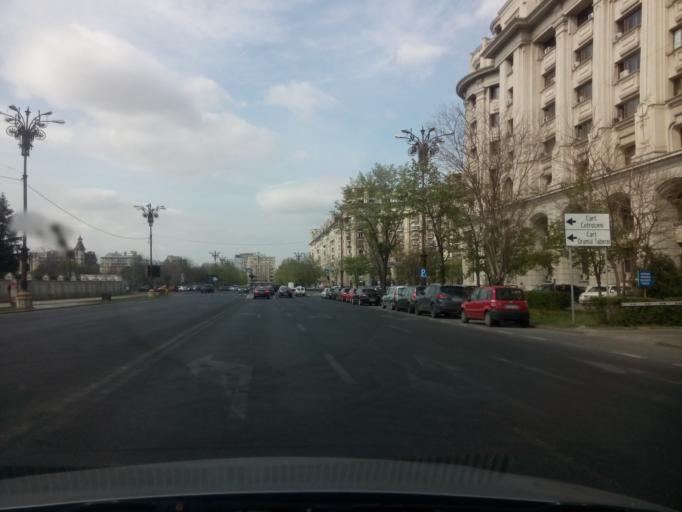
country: RO
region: Bucuresti
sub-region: Municipiul Bucuresti
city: Bucuresti
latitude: 44.4286
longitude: 26.0911
